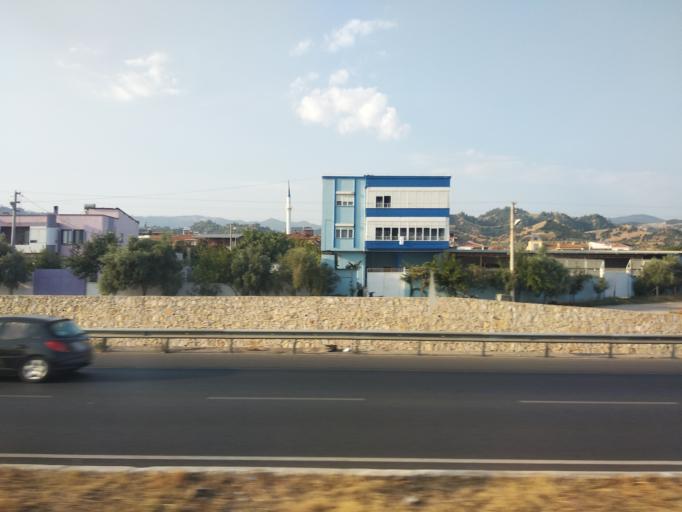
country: TR
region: Manisa
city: Ahmetli
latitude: 38.5060
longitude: 27.9985
